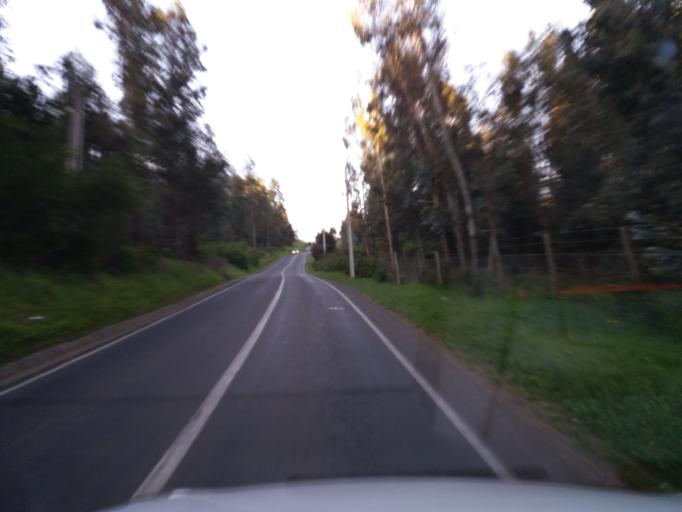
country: CL
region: Valparaiso
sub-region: Provincia de Quillota
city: Quillota
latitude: -32.8853
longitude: -71.2792
